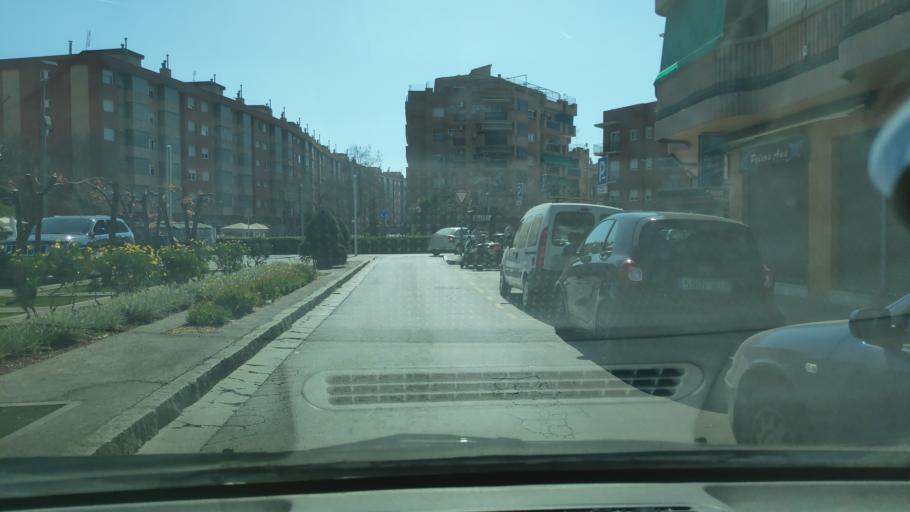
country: ES
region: Catalonia
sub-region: Provincia de Barcelona
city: Mollet del Valles
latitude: 41.5417
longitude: 2.2189
